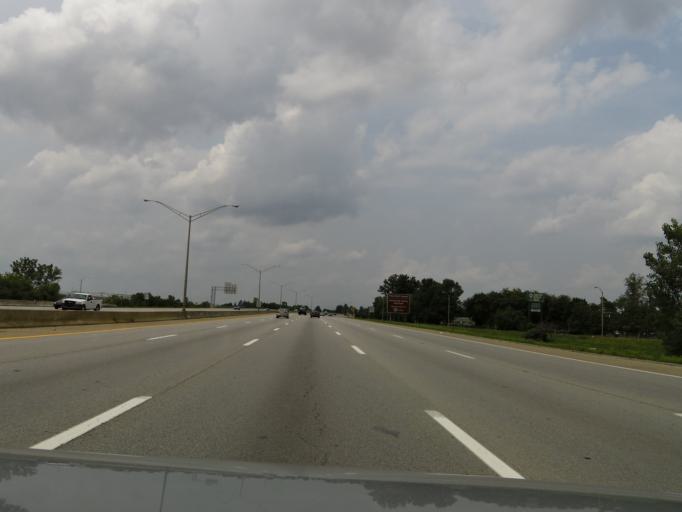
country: US
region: Kentucky
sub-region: Jefferson County
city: Heritage Creek
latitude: 38.1581
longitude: -85.7186
